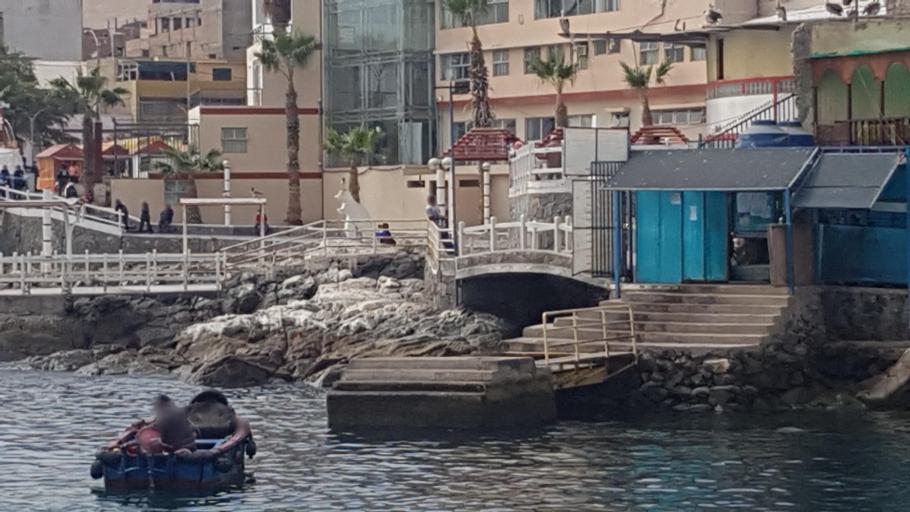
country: PE
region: Moquegua
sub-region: Provincia de Ilo
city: Ilo
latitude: -17.6445
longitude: -71.3468
